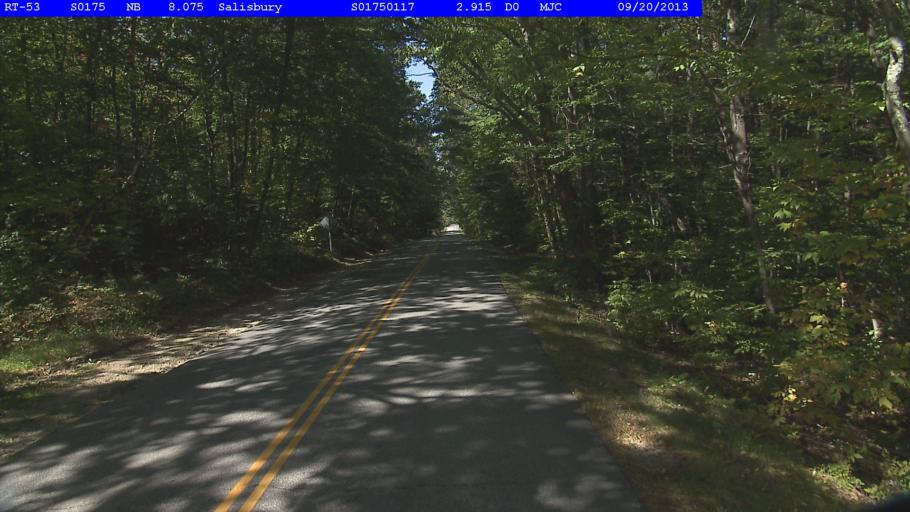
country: US
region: Vermont
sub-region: Rutland County
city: Brandon
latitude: 43.9211
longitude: -73.0886
